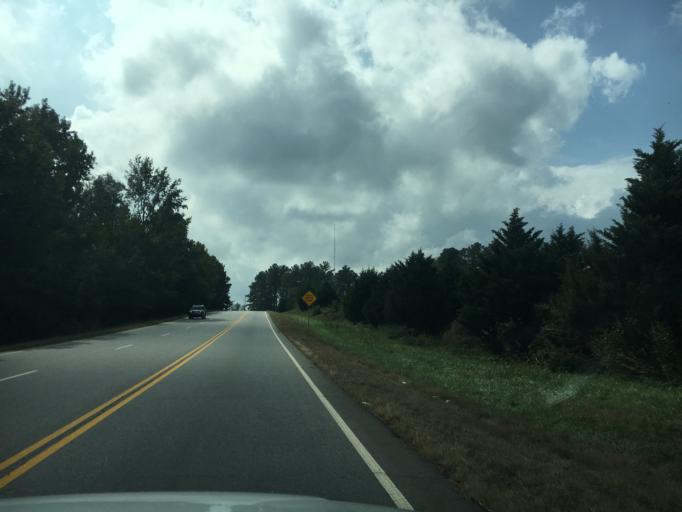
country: US
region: Georgia
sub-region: Franklin County
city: Lavonia
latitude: 34.4010
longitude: -83.1030
